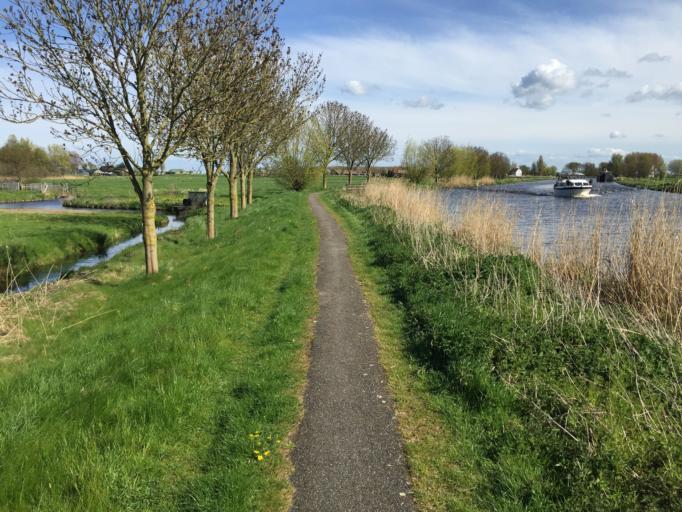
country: NL
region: North Holland
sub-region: Gemeente Aalsmeer
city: Aalsmeer
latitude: 52.2102
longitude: 4.7284
